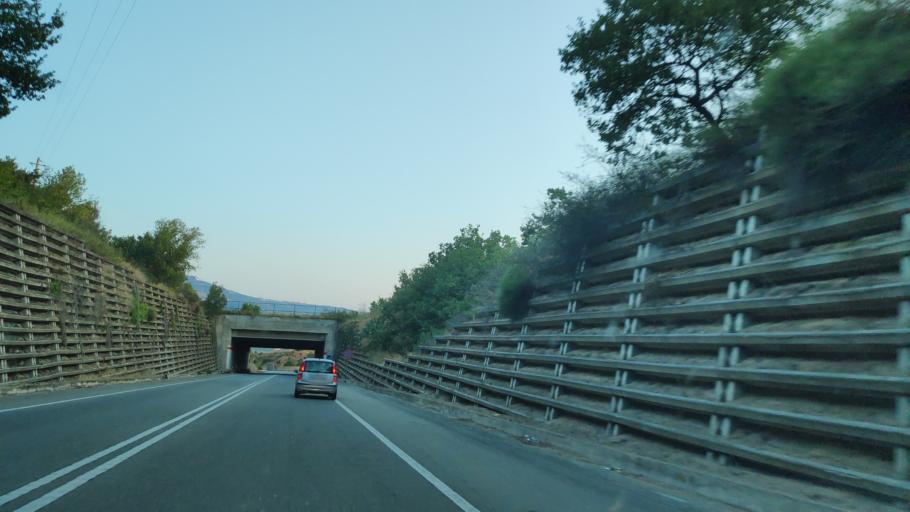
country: IT
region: Calabria
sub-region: Provincia di Catanzaro
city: Soverato Superiore
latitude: 38.6953
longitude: 16.5385
